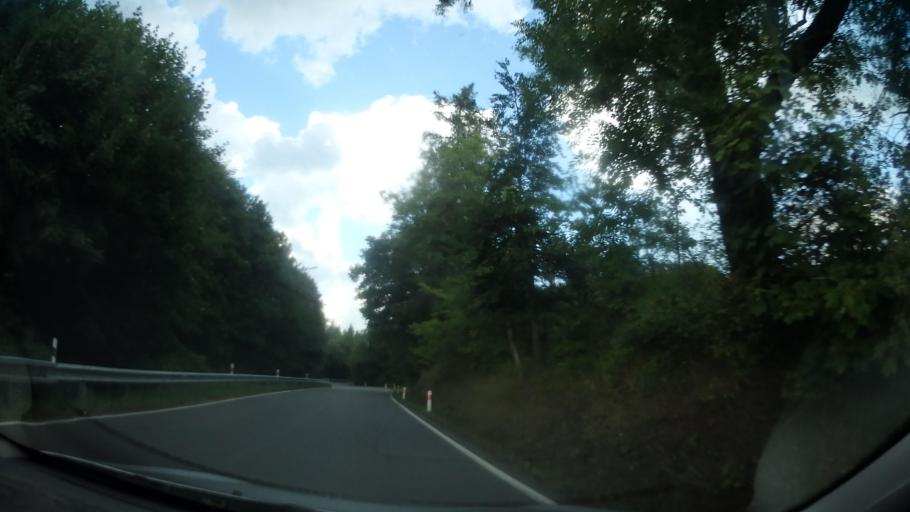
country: CZ
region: Olomoucky
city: Zabreh
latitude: 49.8840
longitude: 16.8103
